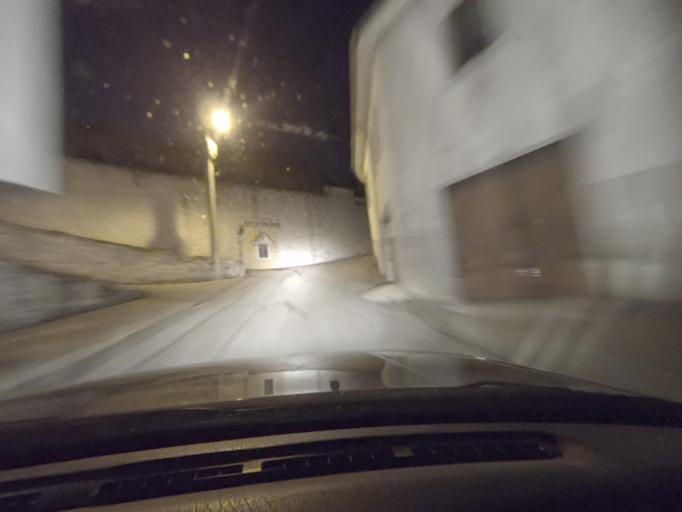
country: PT
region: Vila Real
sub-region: Santa Marta de Penaguiao
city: Santa Marta de Penaguiao
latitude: 41.2237
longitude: -7.8395
